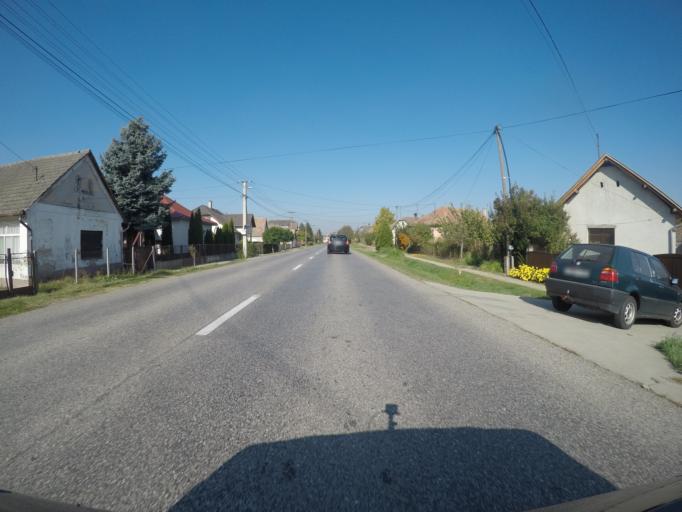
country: HU
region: Tolna
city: Szedres
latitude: 46.4797
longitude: 18.6834
